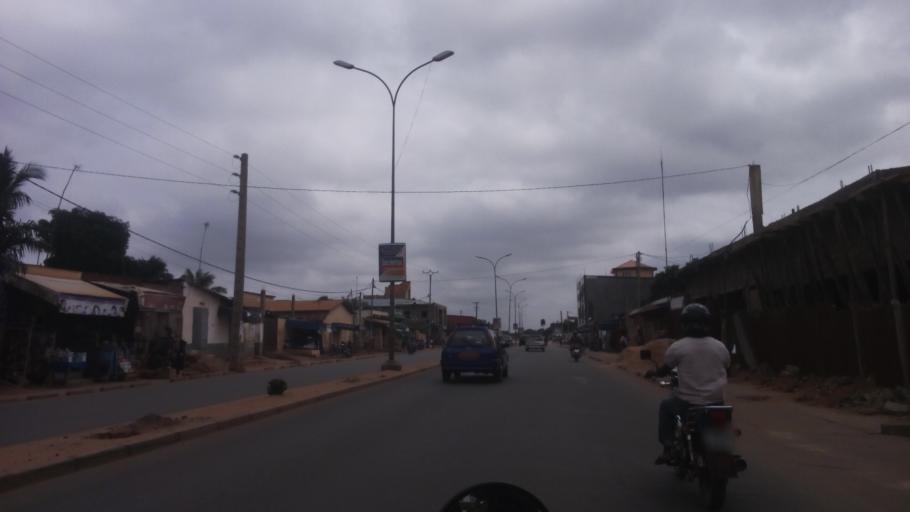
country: TG
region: Maritime
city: Lome
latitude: 6.1932
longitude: 1.1721
